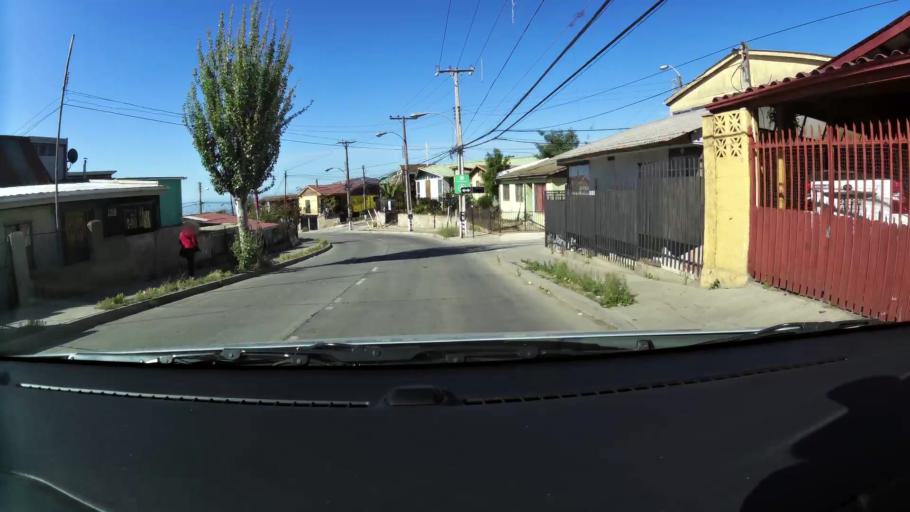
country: CL
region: Valparaiso
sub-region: Provincia de Valparaiso
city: Vina del Mar
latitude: -33.0480
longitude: -71.5600
